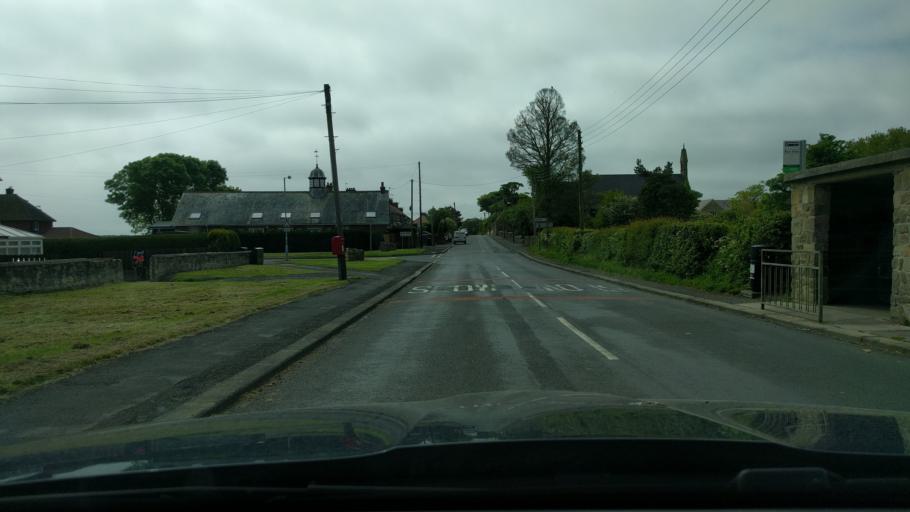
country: GB
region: England
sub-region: Northumberland
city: Acklington
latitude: 55.2931
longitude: -1.6082
